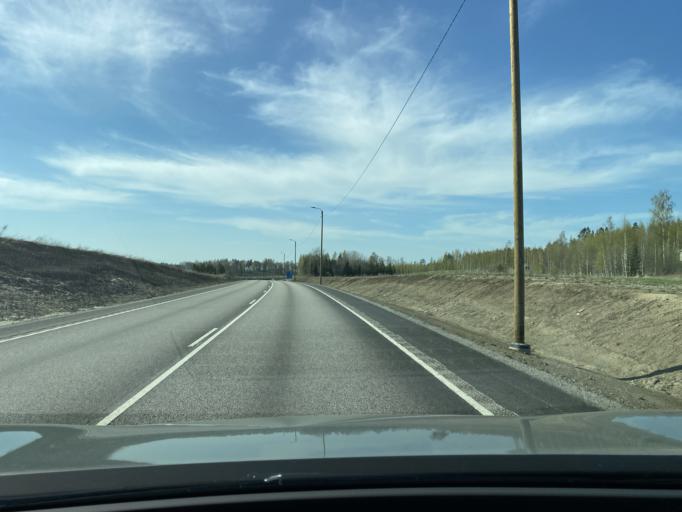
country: FI
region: Uusimaa
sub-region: Helsinki
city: Nurmijaervi
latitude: 60.4216
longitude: 24.7361
